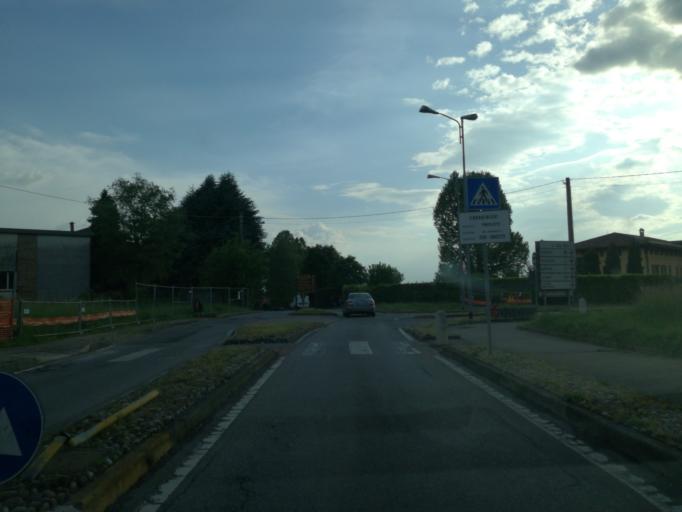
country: IT
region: Lombardy
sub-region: Provincia di Lecco
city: Paderno d'Adda
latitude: 45.6742
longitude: 9.4432
